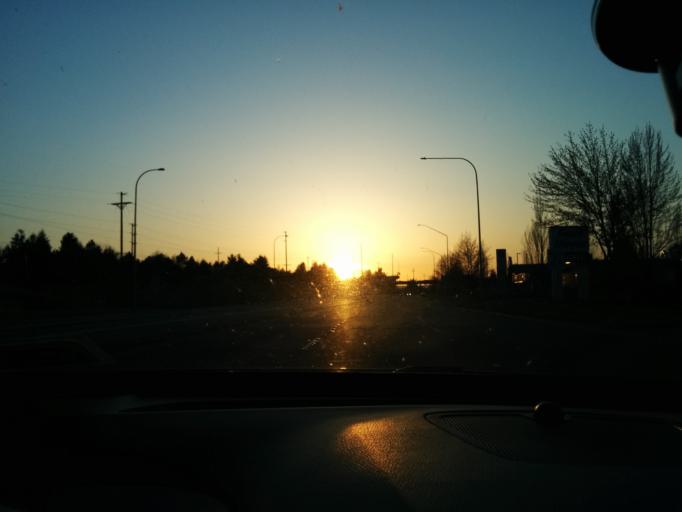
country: US
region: Washington
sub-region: Snohomish County
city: Monroe
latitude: 47.8612
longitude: -121.9780
